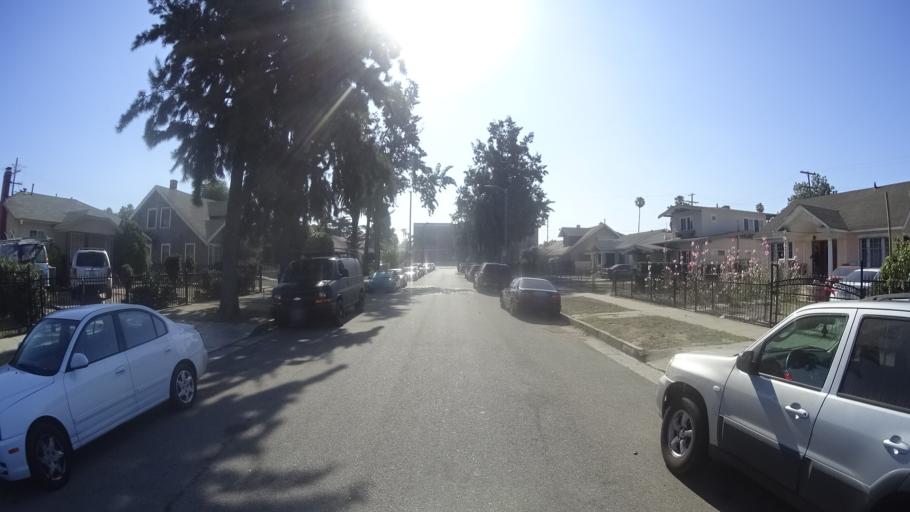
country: US
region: California
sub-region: Los Angeles County
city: Westmont
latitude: 33.9770
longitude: -118.2932
